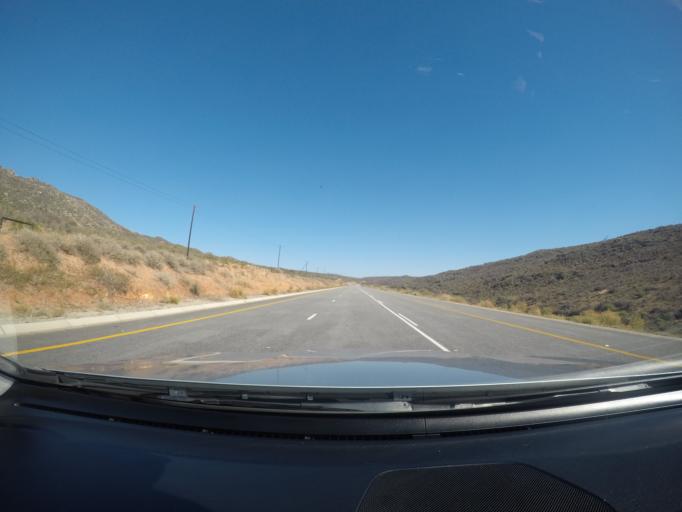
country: ZA
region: Western Cape
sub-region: West Coast District Municipality
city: Clanwilliam
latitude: -32.3449
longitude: 18.9275
